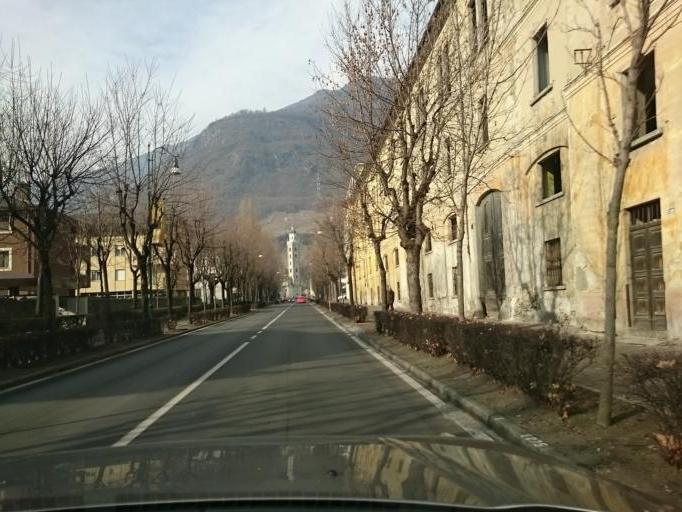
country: IT
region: Lombardy
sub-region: Provincia di Sondrio
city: Tirano
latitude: 46.2175
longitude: 10.1601
